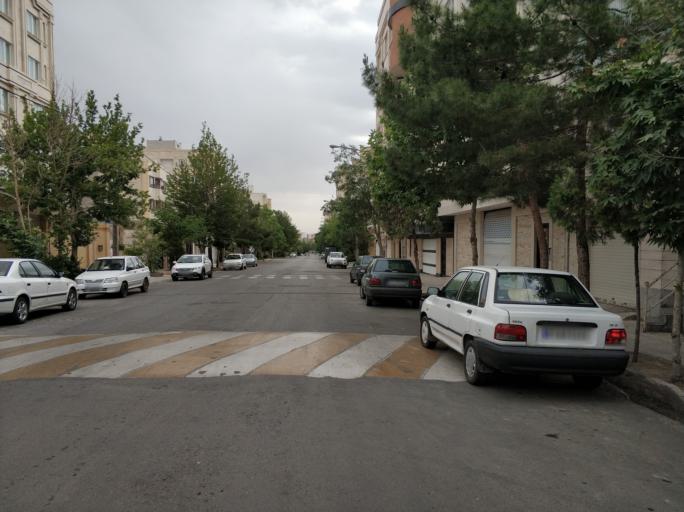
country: IR
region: Razavi Khorasan
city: Torqabeh
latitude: 36.3419
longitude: 59.4651
